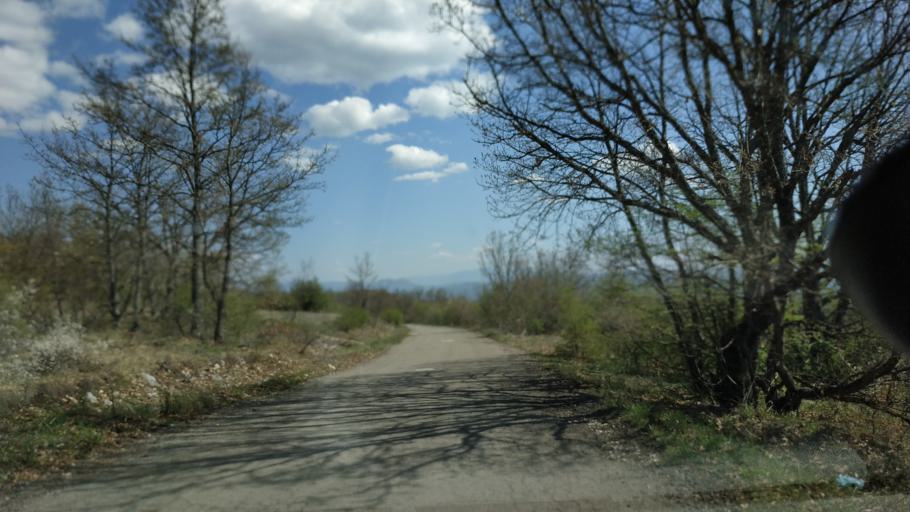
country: RS
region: Central Serbia
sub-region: Zajecarski Okrug
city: Soko Banja
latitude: 43.5543
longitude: 21.8937
